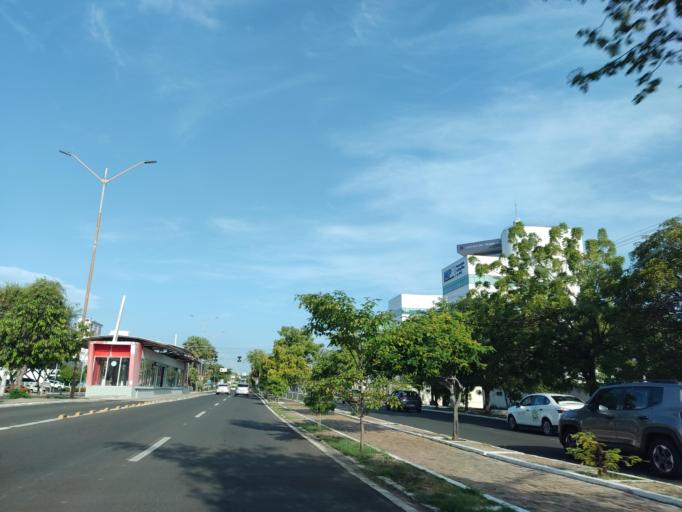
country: BR
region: Piaui
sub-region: Teresina
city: Teresina
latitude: -5.0805
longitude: -42.7865
